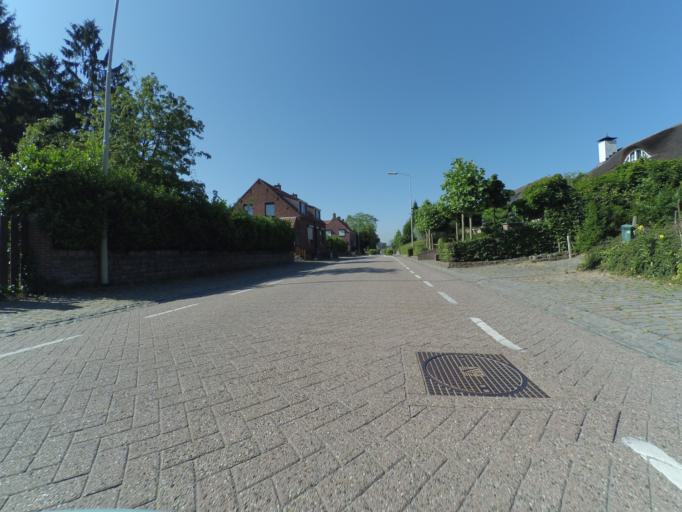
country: NL
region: North Brabant
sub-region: Gemeente Woensdrecht
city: Woensdrecht
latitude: 51.4128
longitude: 4.3184
